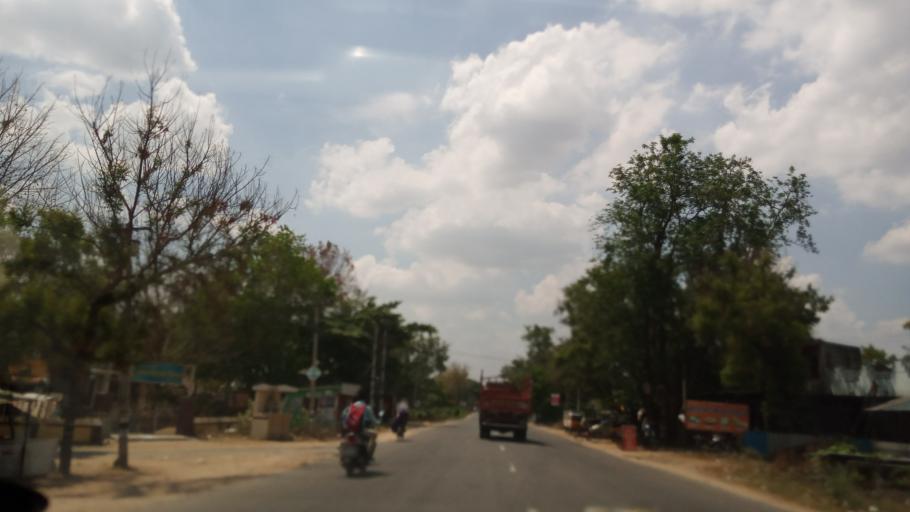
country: IN
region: Tamil Nadu
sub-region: Vellore
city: Arcot
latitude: 12.9763
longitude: 79.2798
